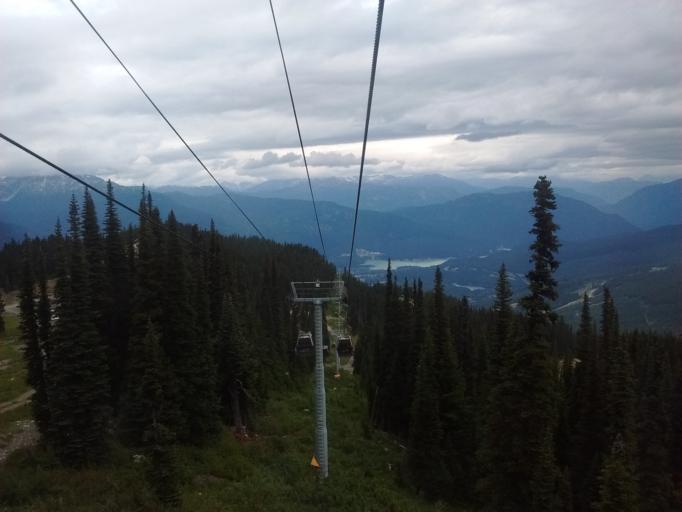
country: CA
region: British Columbia
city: Whistler
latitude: 50.0738
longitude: -122.9477
